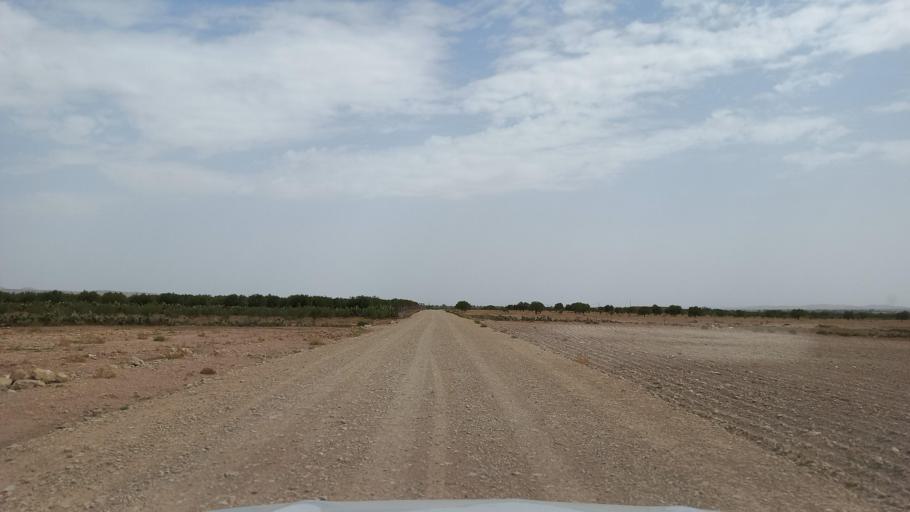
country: TN
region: Al Qasrayn
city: Kasserine
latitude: 35.2804
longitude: 9.0116
